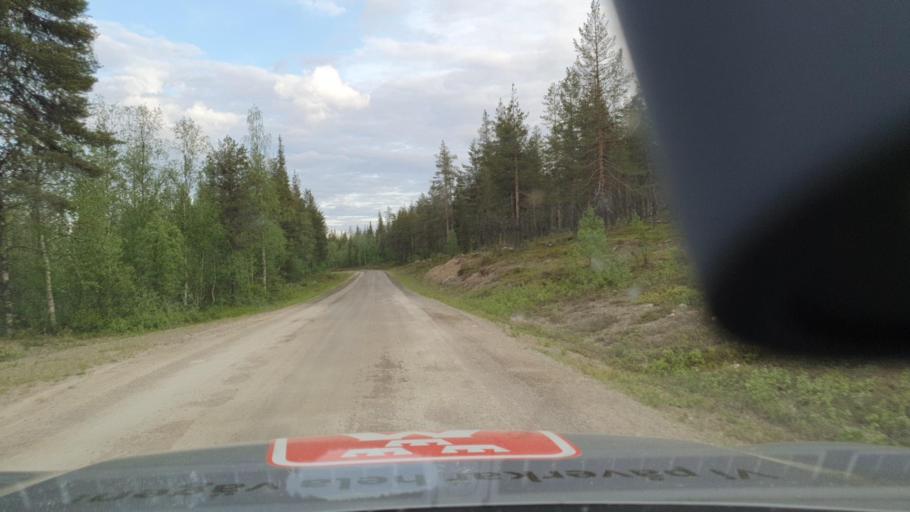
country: SE
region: Norrbotten
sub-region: Gallivare Kommun
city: Gaellivare
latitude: 66.7233
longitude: 21.1478
